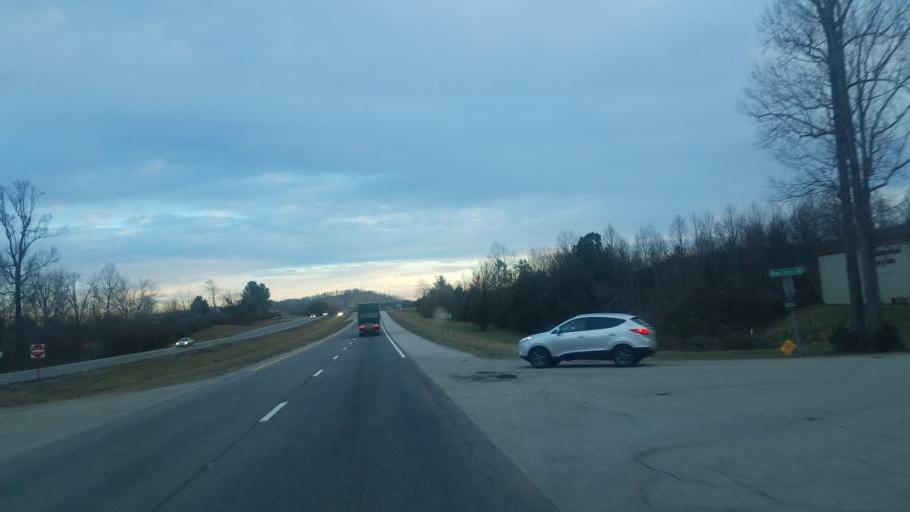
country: US
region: Tennessee
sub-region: Putnam County
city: Cookeville
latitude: 36.1209
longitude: -85.4889
